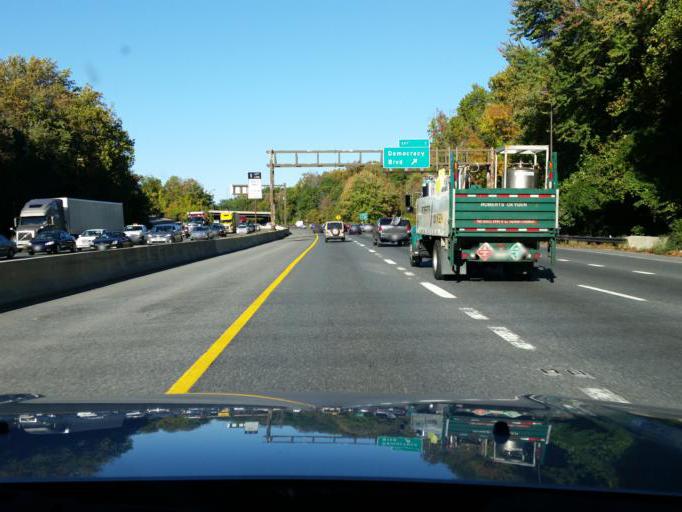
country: US
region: Maryland
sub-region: Montgomery County
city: North Bethesda
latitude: 39.0186
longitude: -77.1458
